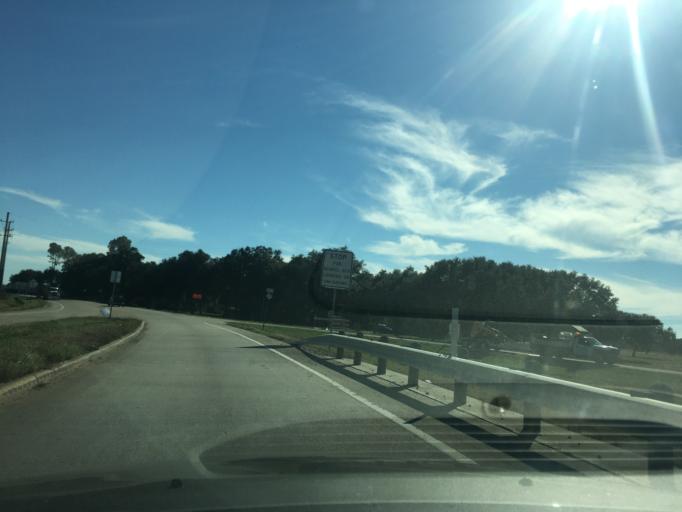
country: US
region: Texas
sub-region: Fort Bend County
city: Needville
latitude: 29.4821
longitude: -95.9368
